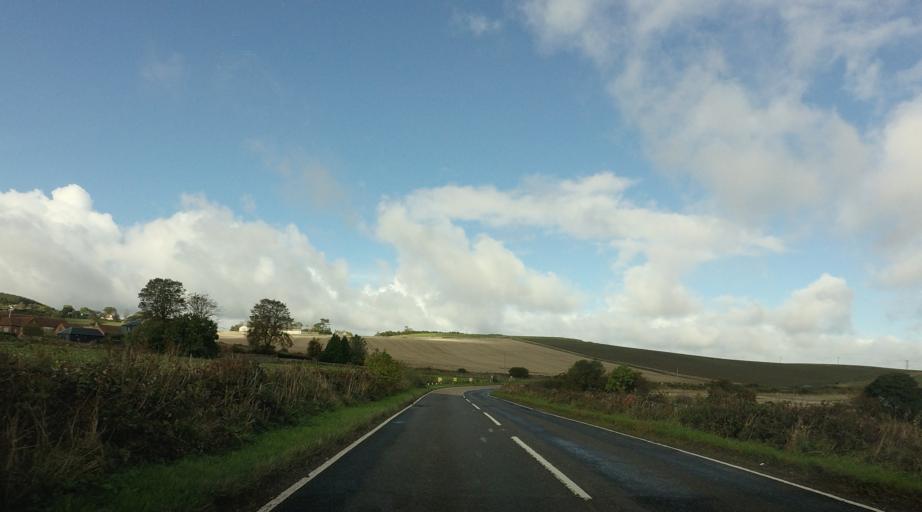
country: GB
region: Scotland
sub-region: Fife
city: Balmullo
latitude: 56.3829
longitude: -2.9231
